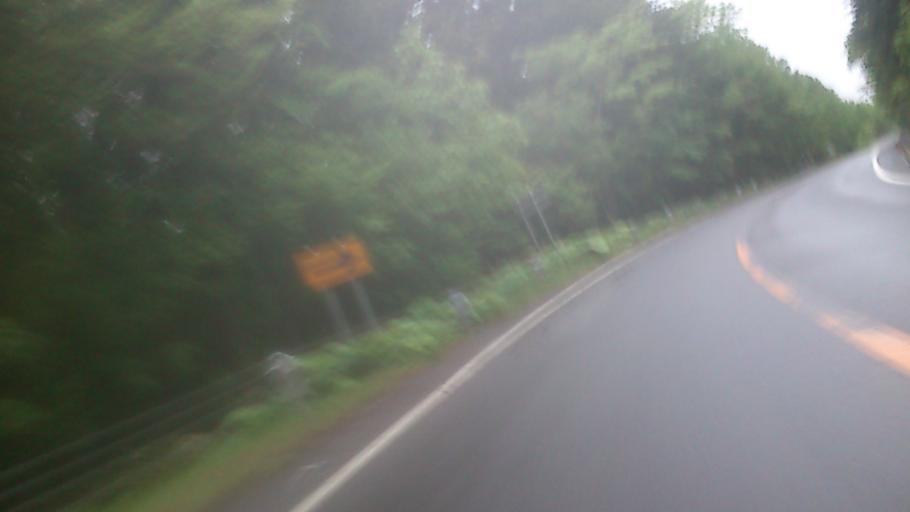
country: JP
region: Hokkaido
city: Tomakomai
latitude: 42.7609
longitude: 141.4266
